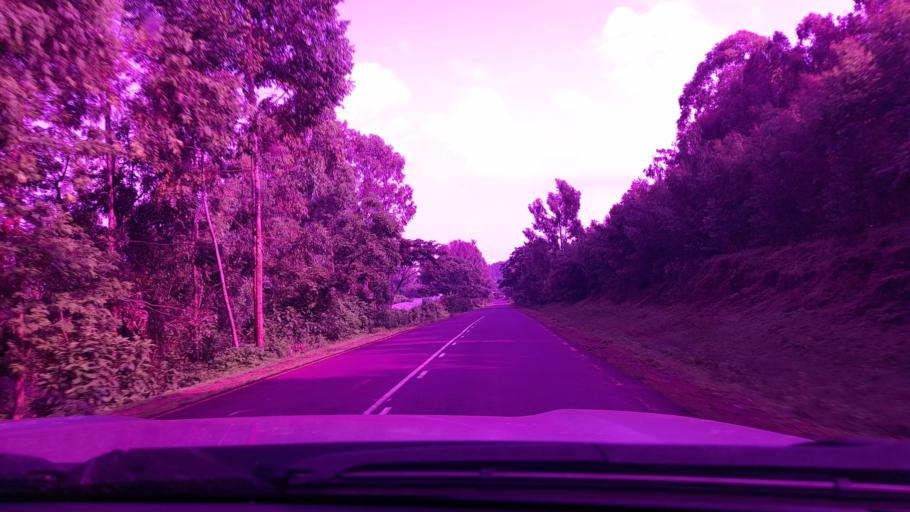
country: ET
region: Oromiya
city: Bedele
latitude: 8.1632
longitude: 36.4738
